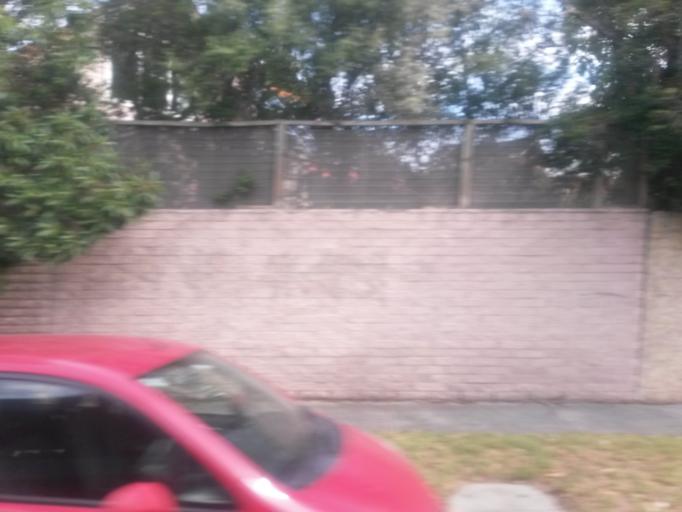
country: AU
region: Victoria
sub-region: Stonnington
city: Glen Iris
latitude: -37.8594
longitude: 145.0567
